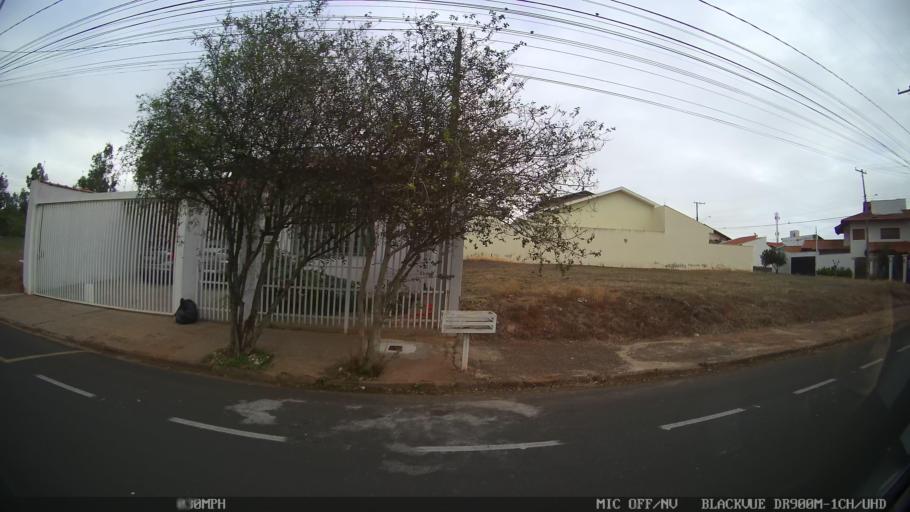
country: BR
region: Sao Paulo
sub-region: Sao Jose Do Rio Preto
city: Sao Jose do Rio Preto
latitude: -20.8361
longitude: -49.3951
